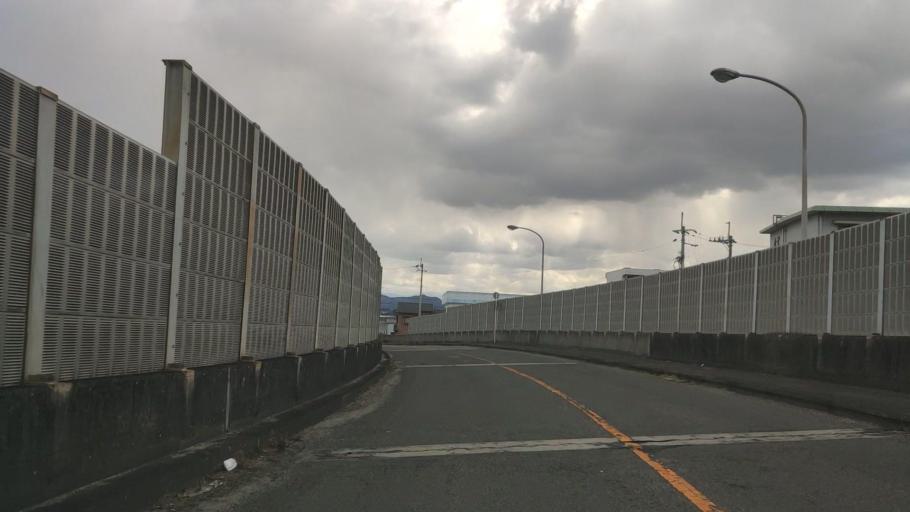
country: JP
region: Ehime
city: Saijo
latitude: 34.0587
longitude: 133.0175
